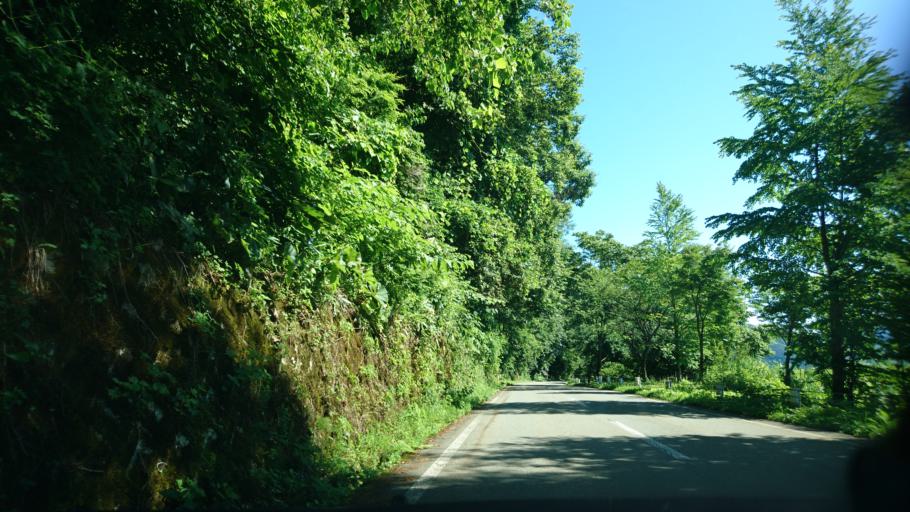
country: JP
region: Akita
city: Kakunodatemachi
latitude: 39.7222
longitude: 140.6280
